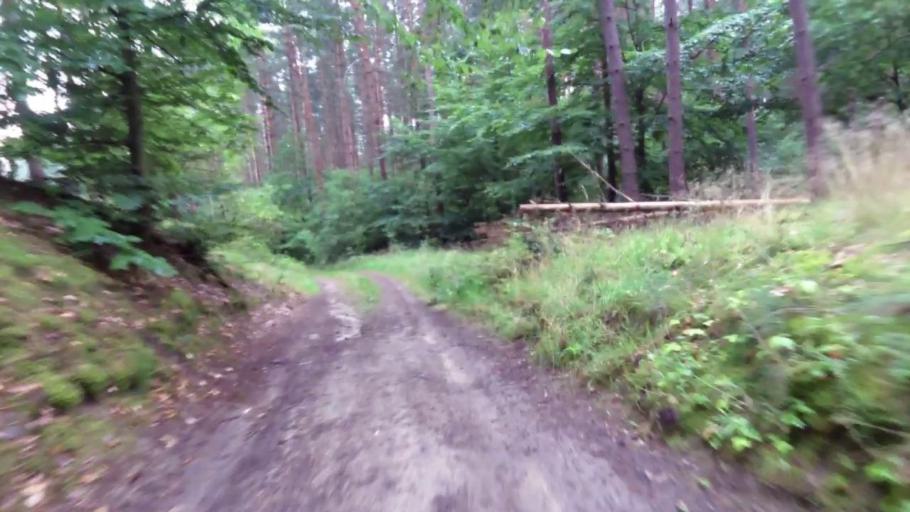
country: PL
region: West Pomeranian Voivodeship
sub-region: Powiat szczecinecki
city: Lubowo
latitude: 53.6075
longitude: 16.3830
